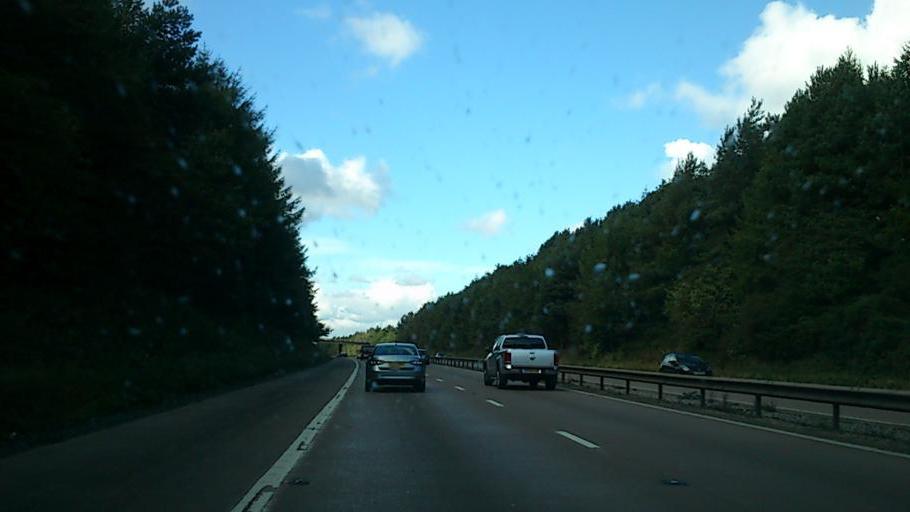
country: GB
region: England
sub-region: Staffordshire
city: Codsall
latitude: 52.6469
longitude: -2.2278
